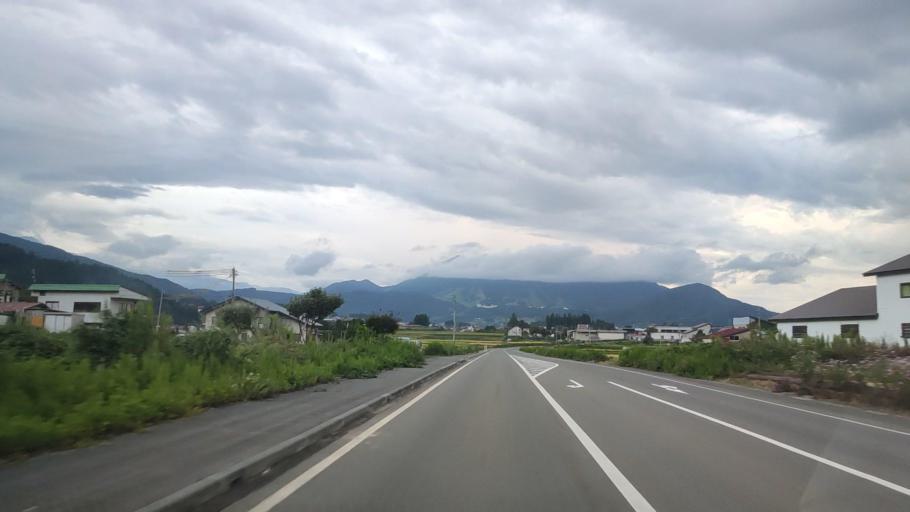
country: JP
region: Nagano
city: Iiyama
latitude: 36.8777
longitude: 138.4097
